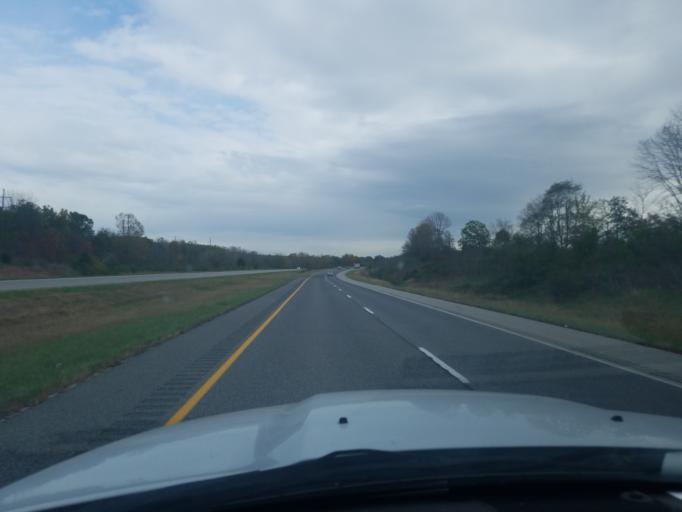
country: US
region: Indiana
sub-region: Warrick County
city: Boonville
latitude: 38.2011
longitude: -87.2447
